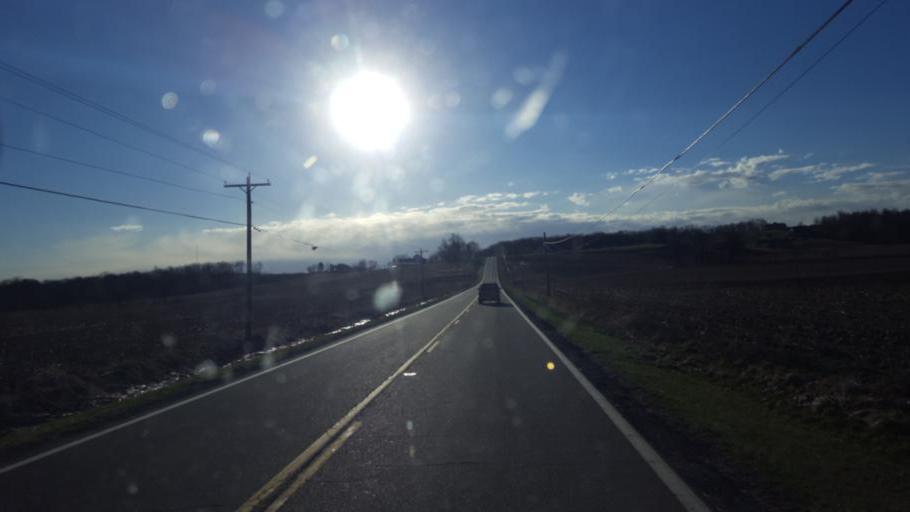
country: US
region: Ohio
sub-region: Wayne County
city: Shreve
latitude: 40.5801
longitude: -82.0394
